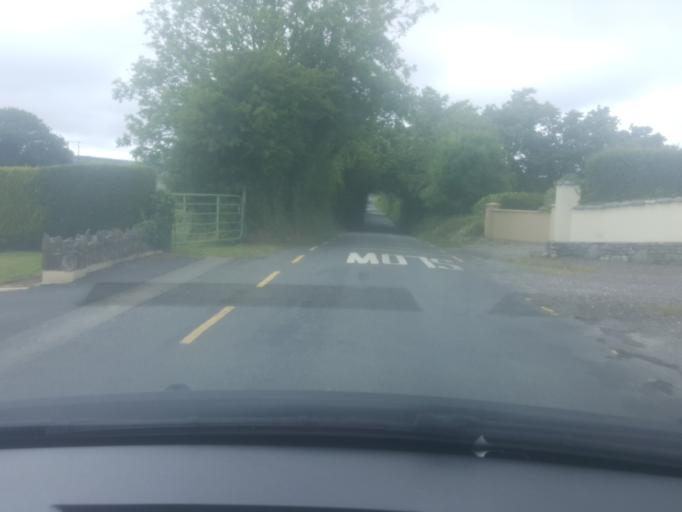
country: IE
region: Munster
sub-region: Ciarrai
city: Cill Airne
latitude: 52.1075
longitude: -9.5058
